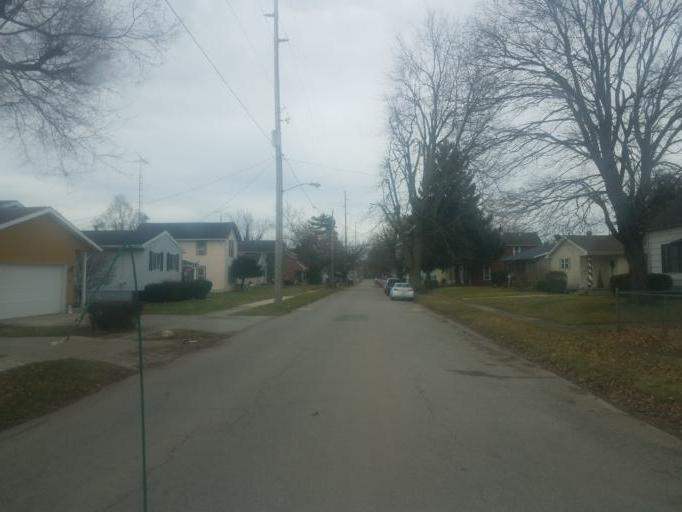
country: US
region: Ohio
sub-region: Marion County
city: Marion
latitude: 40.5928
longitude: -83.1056
